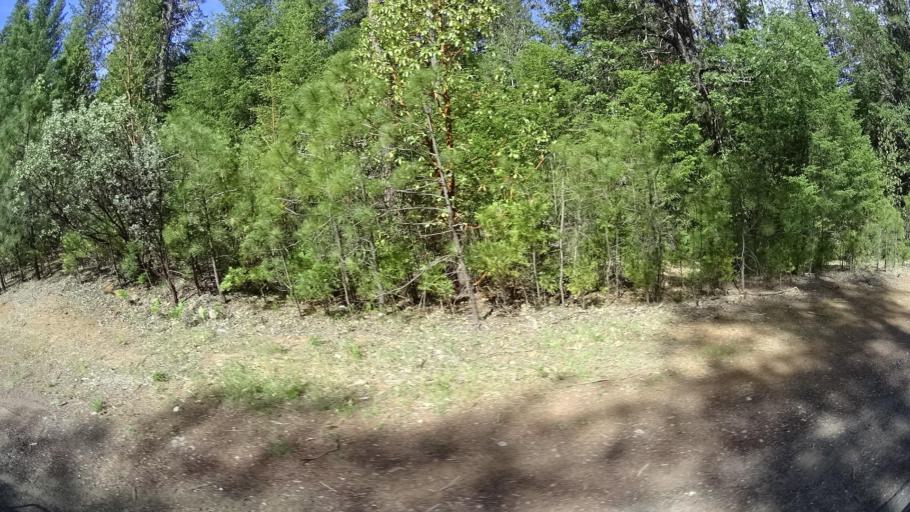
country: US
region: California
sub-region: Lake County
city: Cobb
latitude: 38.8738
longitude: -122.7255
